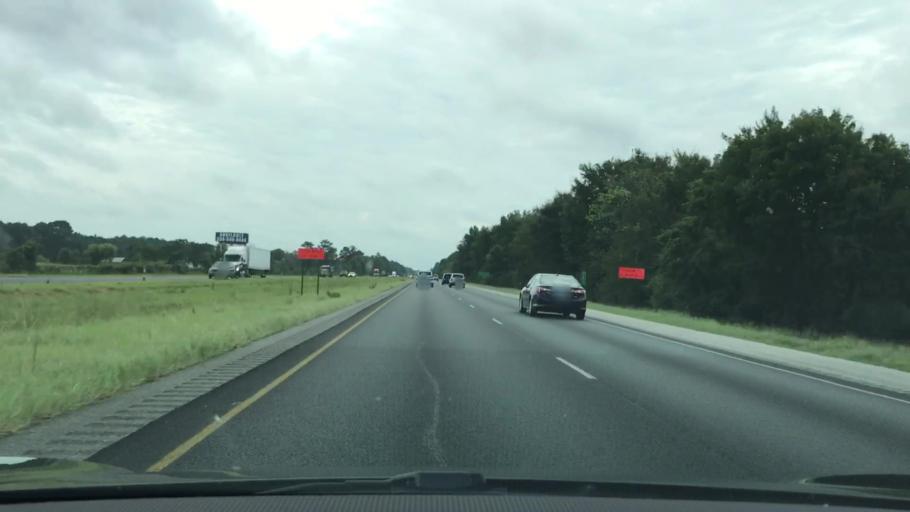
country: US
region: Alabama
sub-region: Montgomery County
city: Pike Road
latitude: 32.3729
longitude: -86.0380
